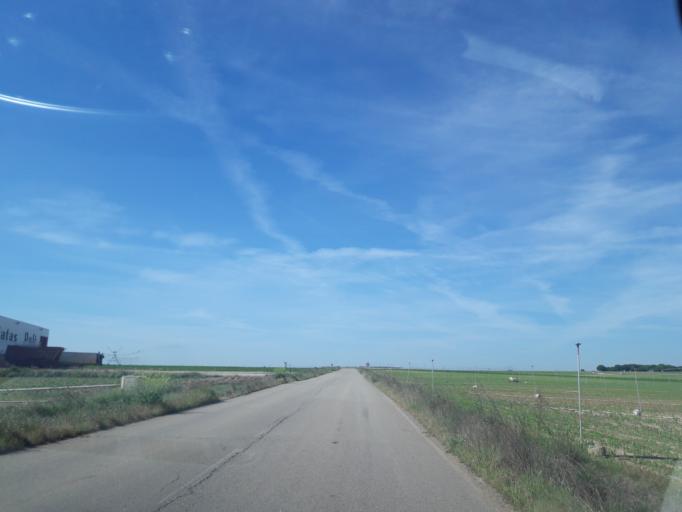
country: ES
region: Castille and Leon
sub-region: Provincia de Salamanca
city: Villoruela
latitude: 41.0356
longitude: -5.3890
